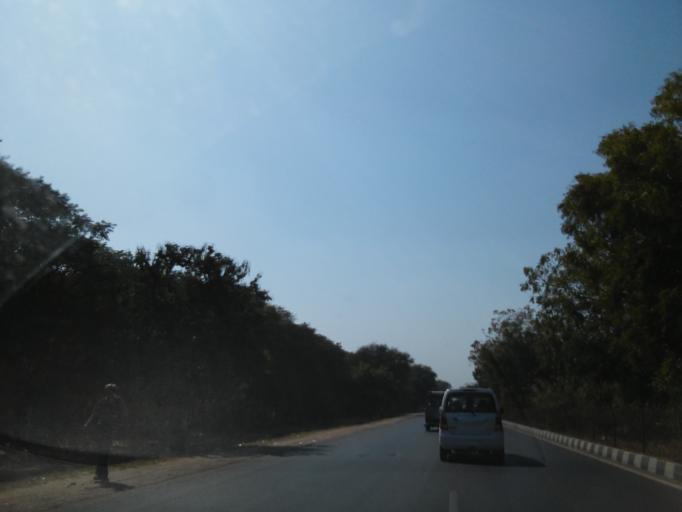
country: IN
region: Gujarat
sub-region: Gandhinagar
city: Adalaj
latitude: 23.1682
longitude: 72.5699
